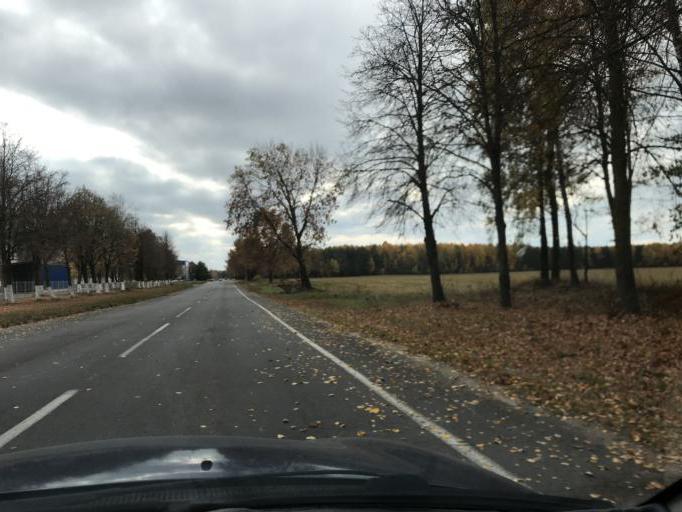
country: BY
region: Grodnenskaya
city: Lida
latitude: 53.9445
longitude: 25.2459
